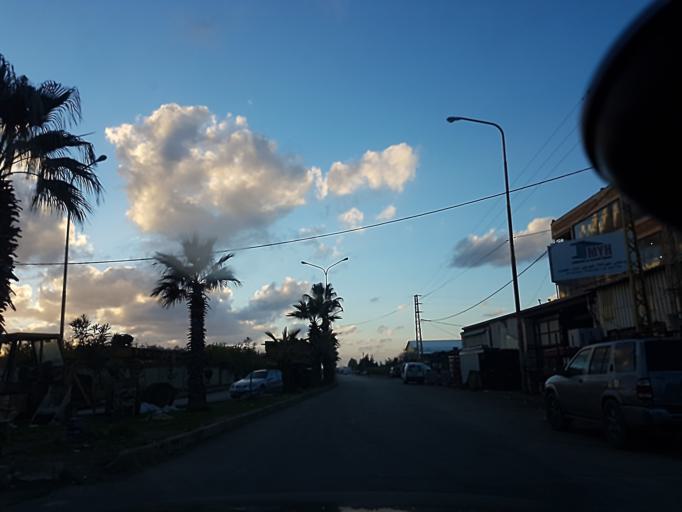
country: LB
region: Liban-Sud
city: Sidon
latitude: 33.5402
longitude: 35.3680
